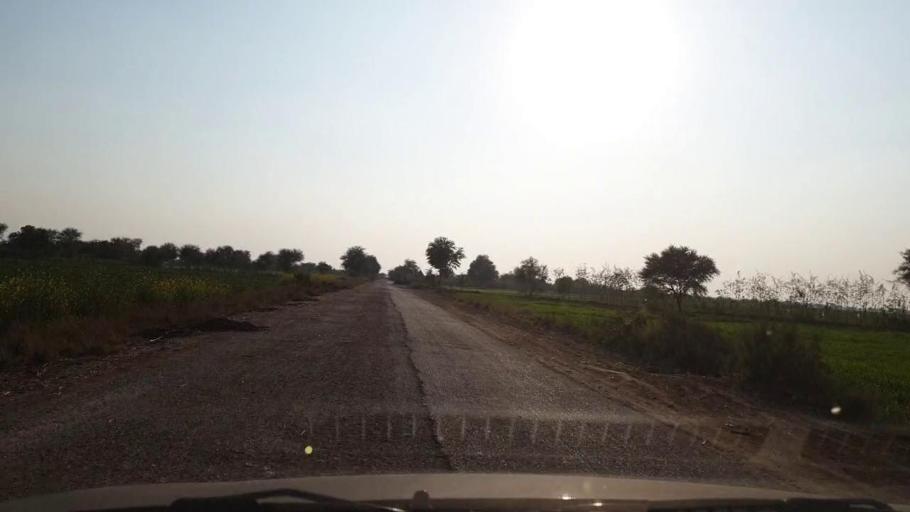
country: PK
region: Sindh
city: Jhol
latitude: 25.9318
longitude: 68.9103
